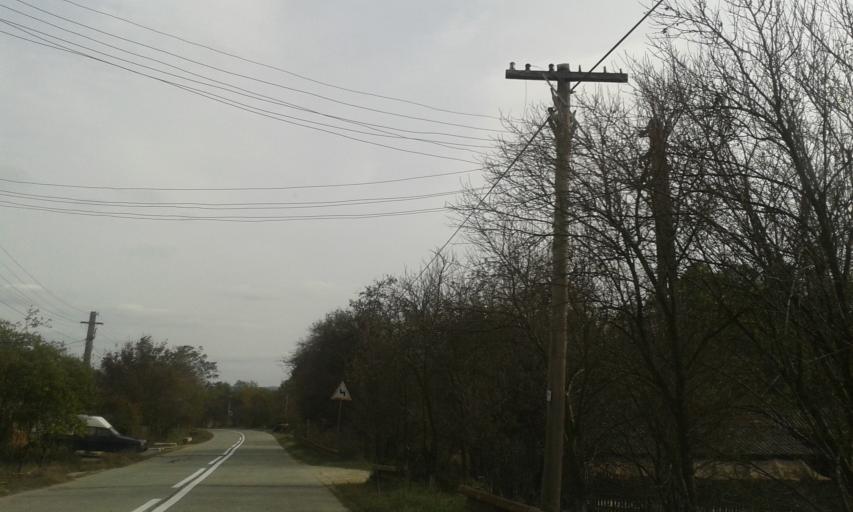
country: RO
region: Valcea
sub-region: Comuna Gradistea
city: Gradistea
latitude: 44.9043
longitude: 23.7978
